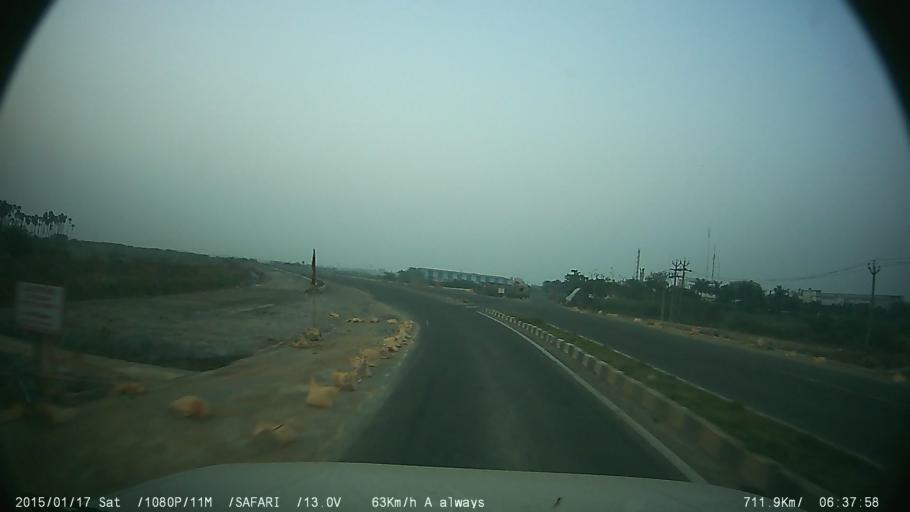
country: IN
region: Tamil Nadu
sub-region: Kancheepuram
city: Sriperumbudur
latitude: 12.9408
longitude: 79.9357
